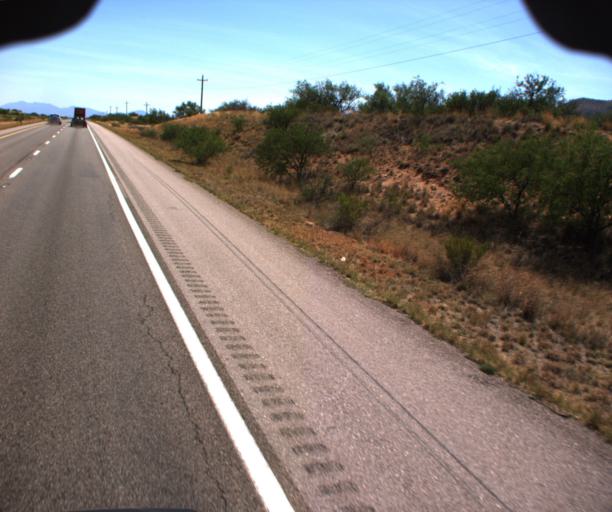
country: US
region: Arizona
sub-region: Cochise County
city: Whetstone
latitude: 31.8779
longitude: -110.3414
